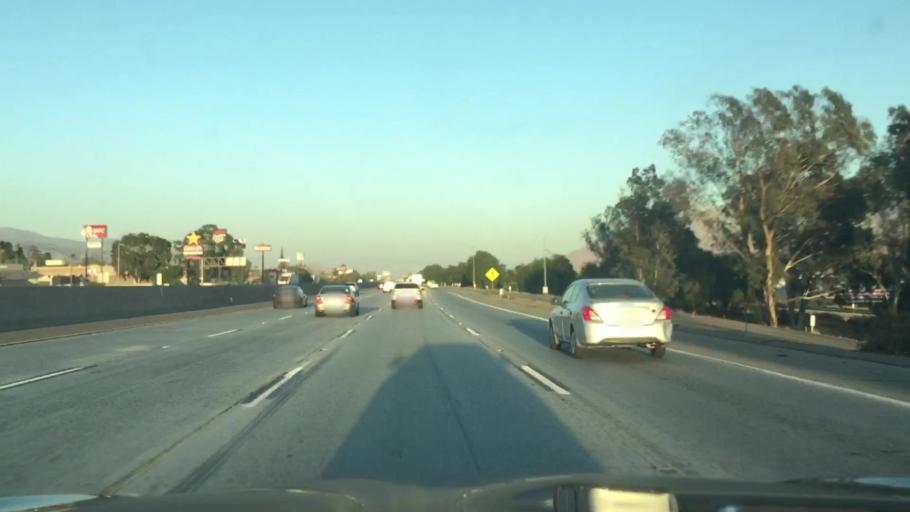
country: US
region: California
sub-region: Riverside County
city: Banning
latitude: 33.9247
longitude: -116.8996
